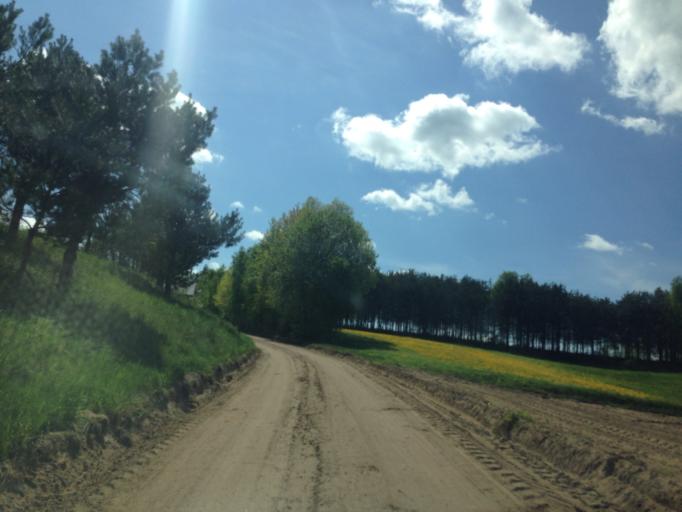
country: PL
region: Kujawsko-Pomorskie
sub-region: Powiat brodnicki
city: Brzozie
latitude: 53.3002
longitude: 19.6573
